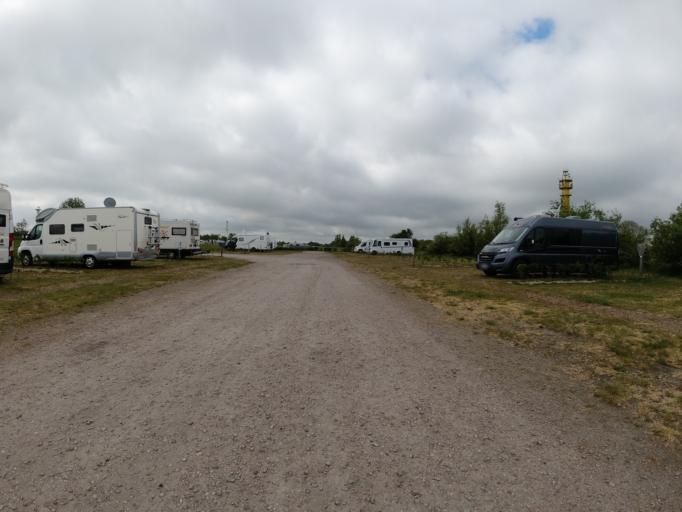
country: DE
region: Lower Saxony
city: Schillig
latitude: 53.7006
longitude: 8.0237
